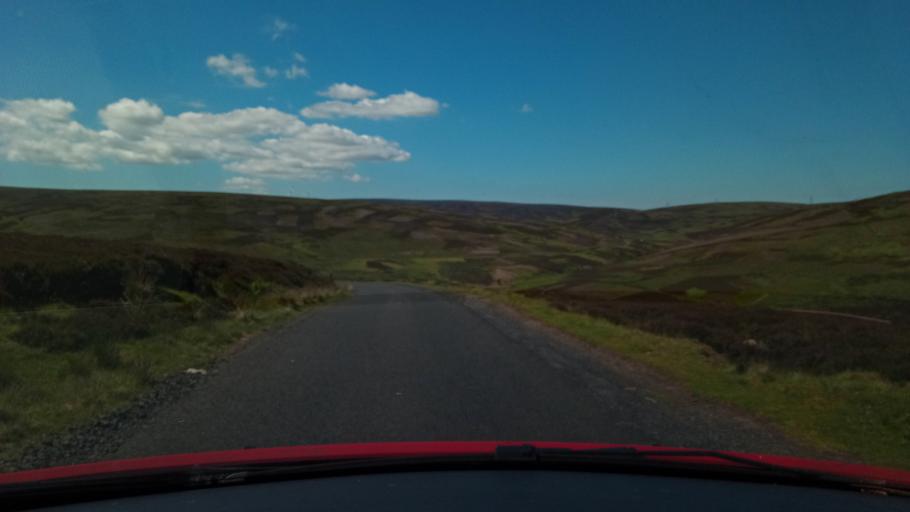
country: GB
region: Scotland
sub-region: East Lothian
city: East Linton
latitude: 55.8452
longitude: -2.5729
